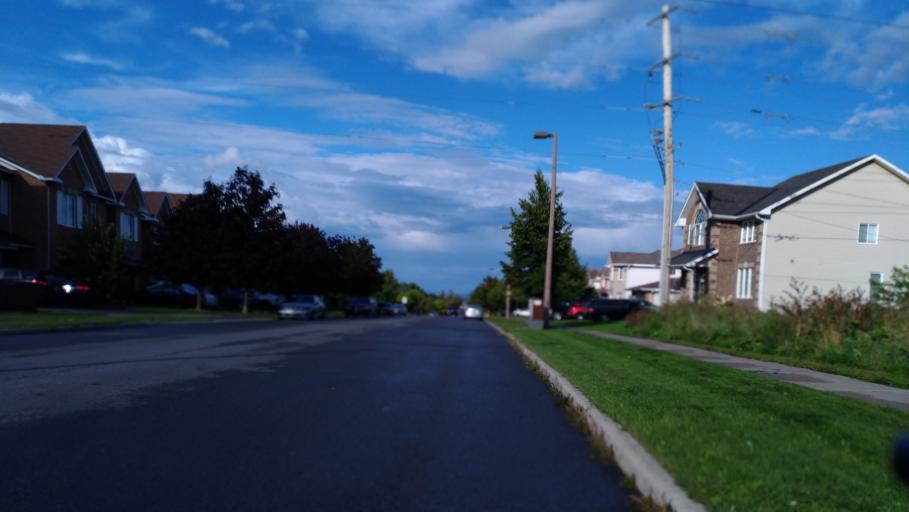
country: CA
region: Ontario
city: Bells Corners
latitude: 45.3480
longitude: -75.9435
